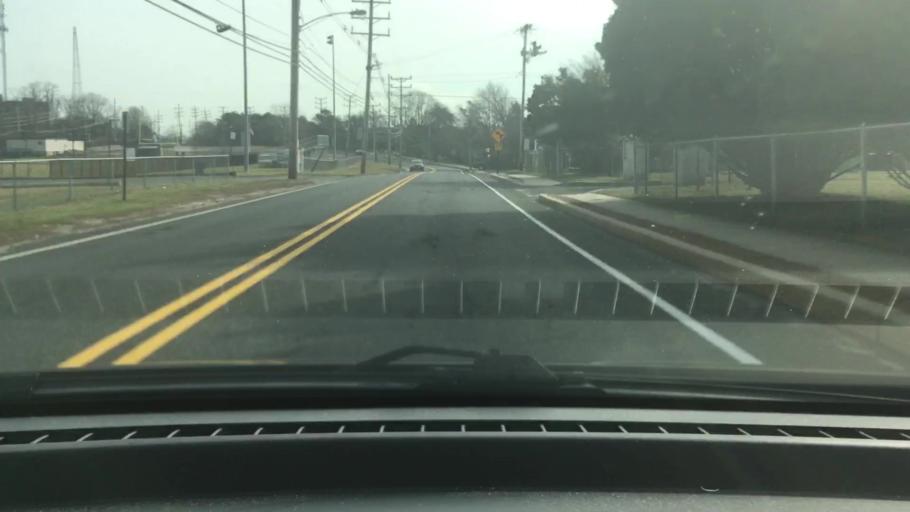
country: US
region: New Jersey
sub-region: Monmouth County
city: Shark River Hills
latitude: 40.2191
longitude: -74.0475
